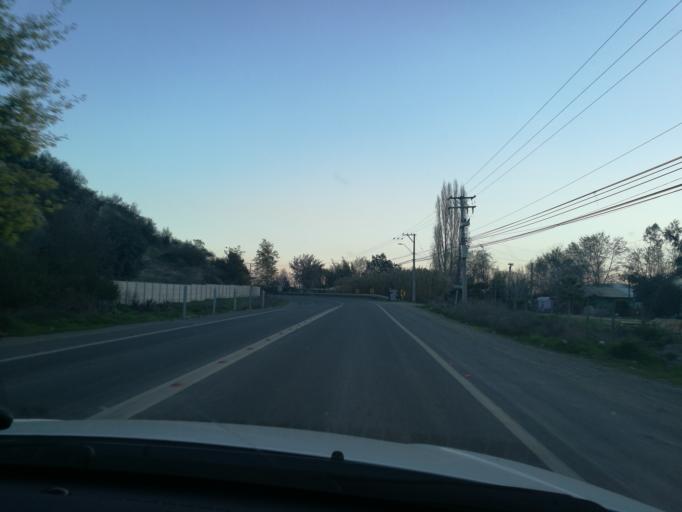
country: CL
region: O'Higgins
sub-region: Provincia de Cachapoal
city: Graneros
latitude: -34.0474
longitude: -70.7265
